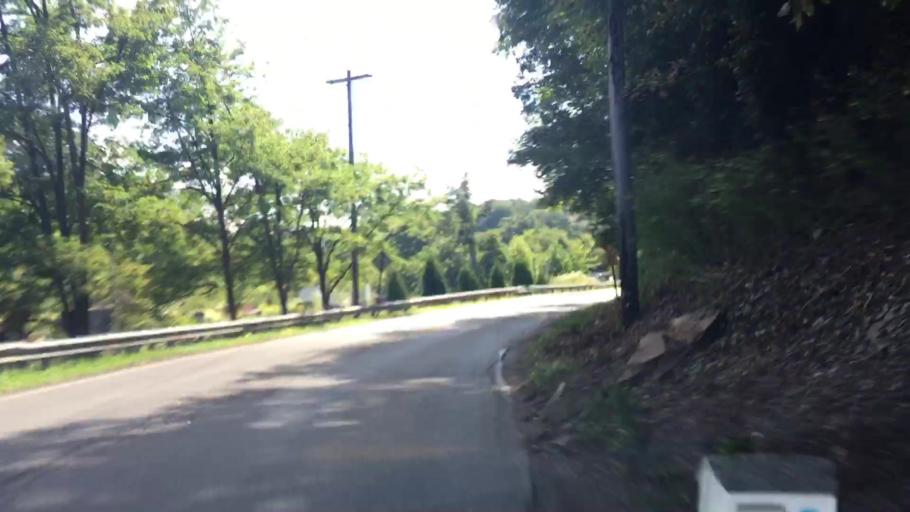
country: US
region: Pennsylvania
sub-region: Allegheny County
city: Enlow
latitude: 40.4526
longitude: -80.2069
